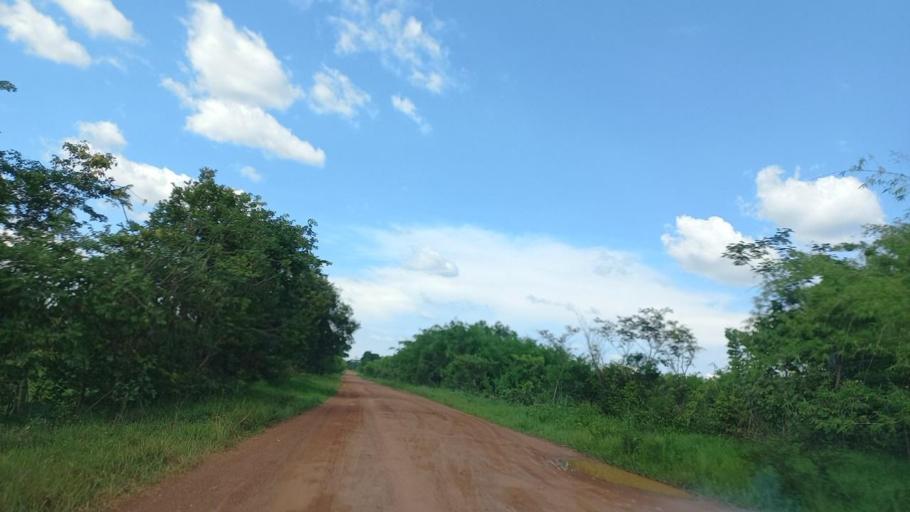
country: ZM
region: Copperbelt
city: Kitwe
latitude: -12.8518
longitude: 28.3904
